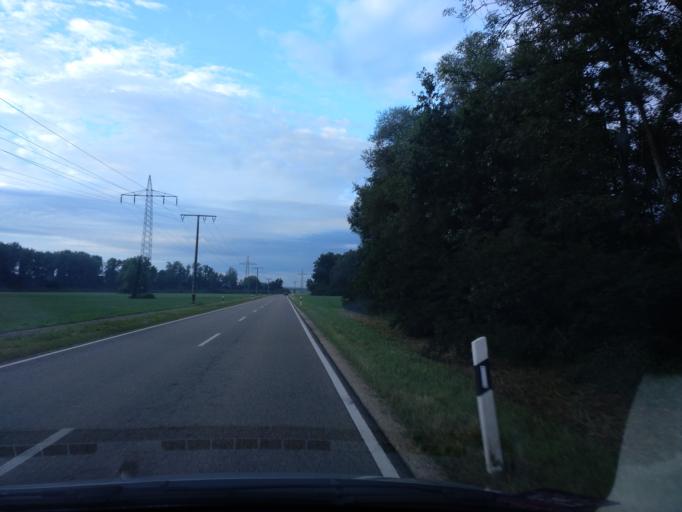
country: DE
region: Bavaria
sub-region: Upper Bavaria
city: Burgheim
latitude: 48.7274
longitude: 11.0155
